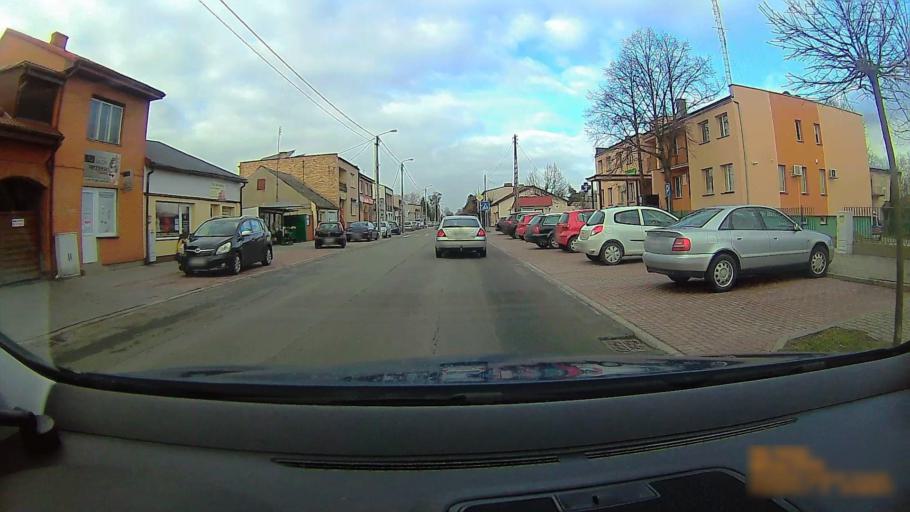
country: PL
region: Greater Poland Voivodeship
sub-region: Powiat koninski
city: Rychwal
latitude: 52.0709
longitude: 18.1657
